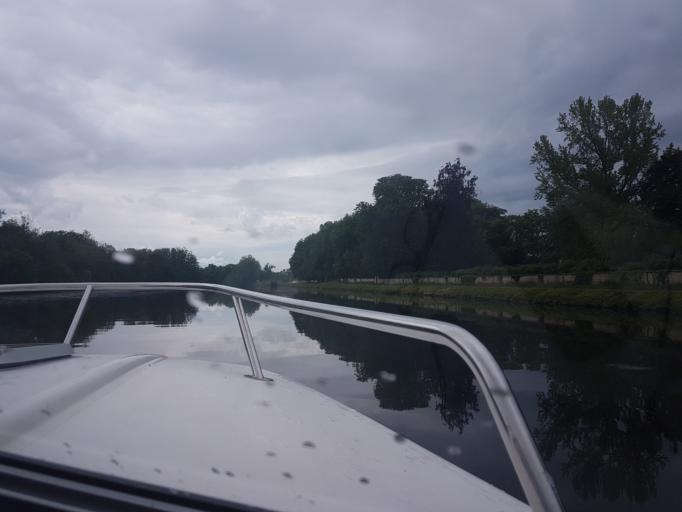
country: FR
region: Bourgogne
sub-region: Departement de l'Yonne
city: Saint-Bris-le-Vineux
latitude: 47.7007
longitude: 3.6380
